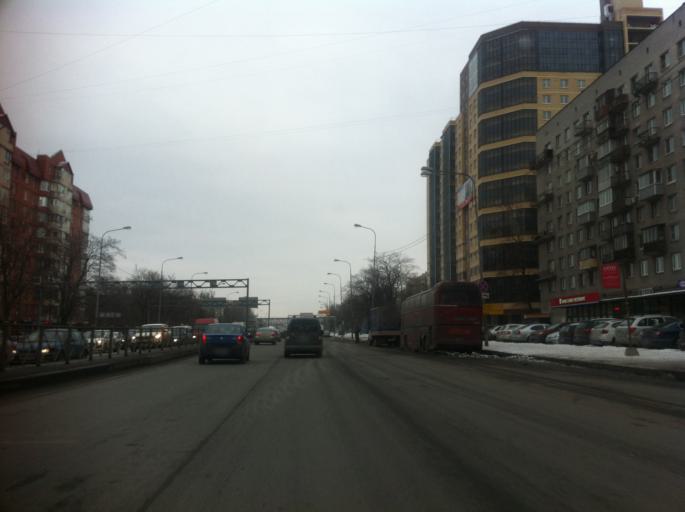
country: RU
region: St.-Petersburg
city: Dachnoye
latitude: 59.8412
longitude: 30.2561
